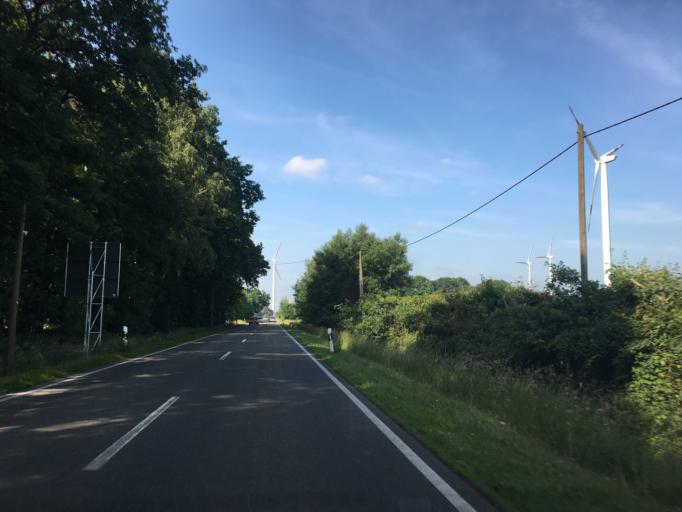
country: DE
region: North Rhine-Westphalia
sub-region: Regierungsbezirk Munster
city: Steinfurt
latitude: 52.1706
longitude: 7.3843
